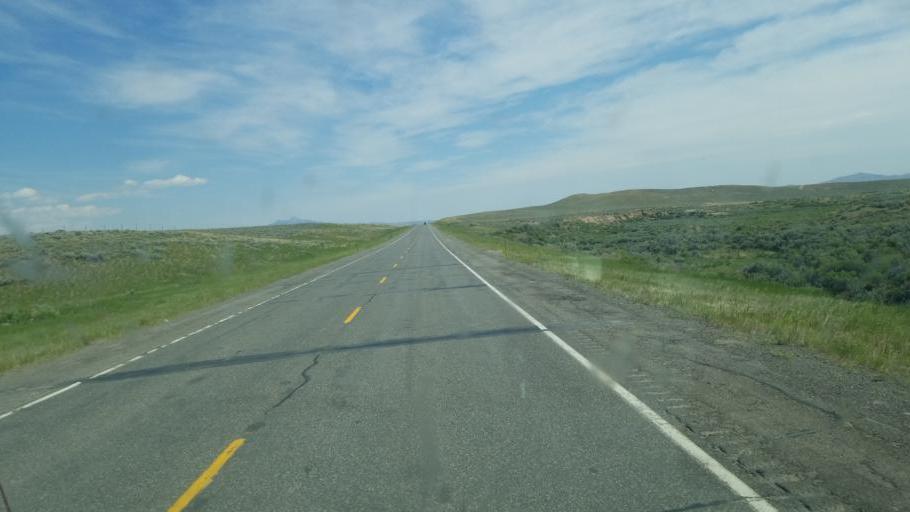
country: US
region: Wyoming
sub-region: Park County
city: Cody
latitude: 44.4233
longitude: -109.0101
